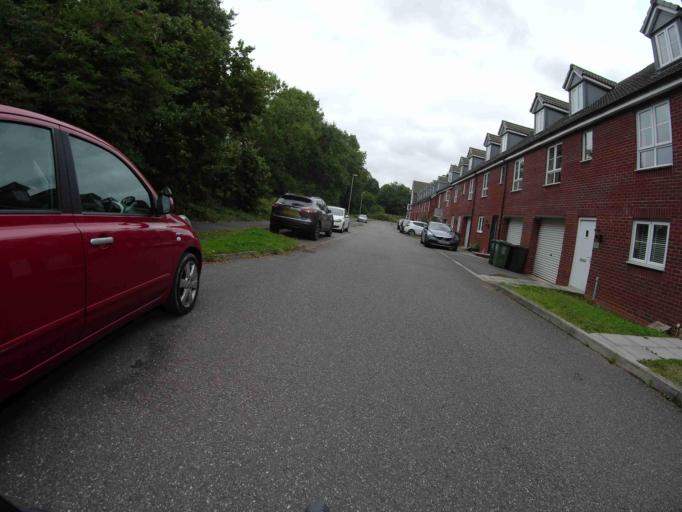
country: GB
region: England
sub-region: Devon
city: Topsham
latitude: 50.6997
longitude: -3.4727
